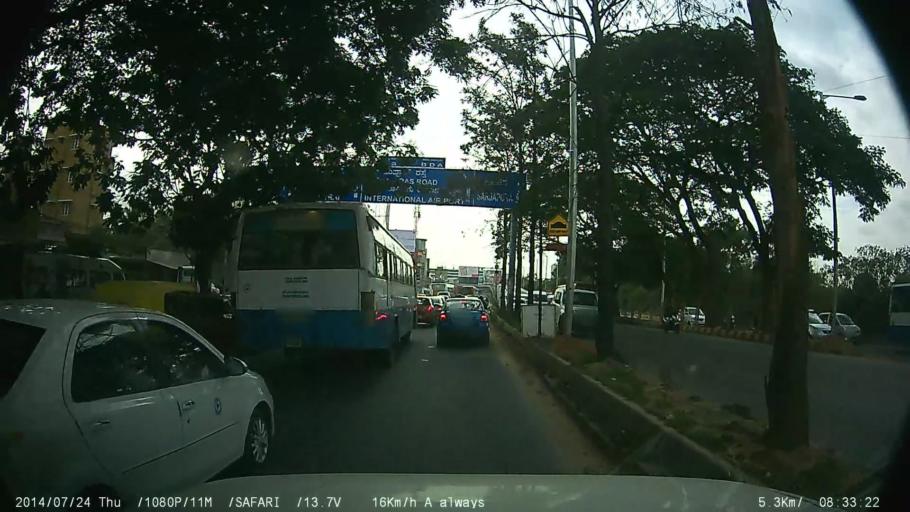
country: IN
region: Karnataka
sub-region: Bangalore Urban
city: Bangalore
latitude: 12.9215
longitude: 77.6619
